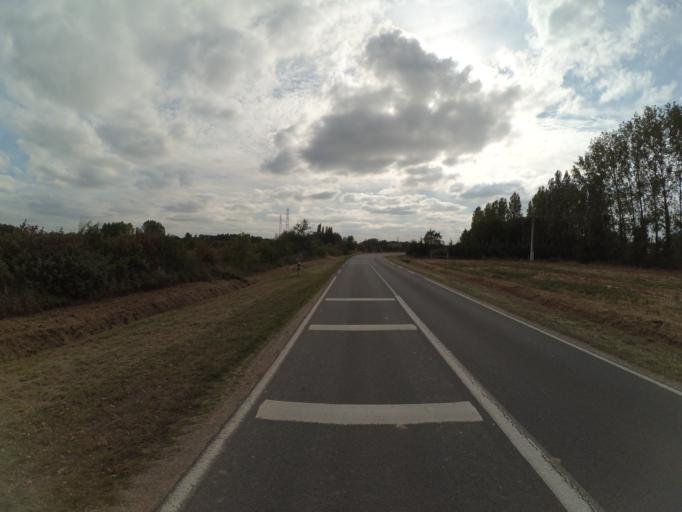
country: FR
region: Centre
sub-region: Departement d'Indre-et-Loire
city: Montlouis-sur-Loire
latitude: 47.4065
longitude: 0.8225
